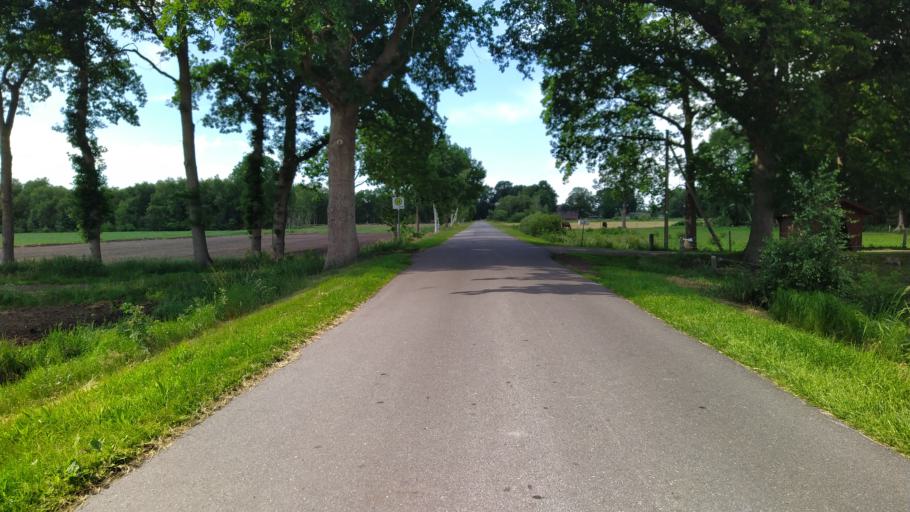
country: DE
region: Lower Saxony
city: Odisheim
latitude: 53.6546
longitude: 8.9359
